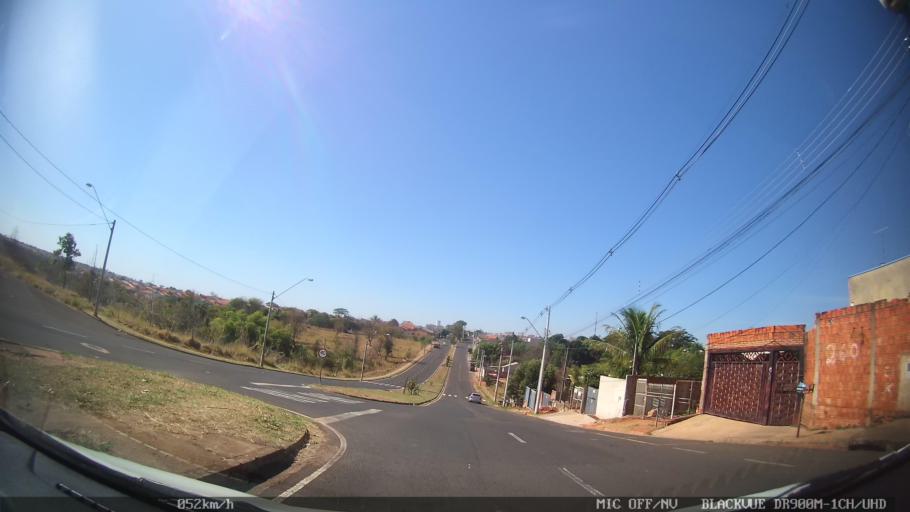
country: BR
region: Sao Paulo
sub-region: Sao Jose Do Rio Preto
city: Sao Jose do Rio Preto
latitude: -20.7666
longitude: -49.4170
